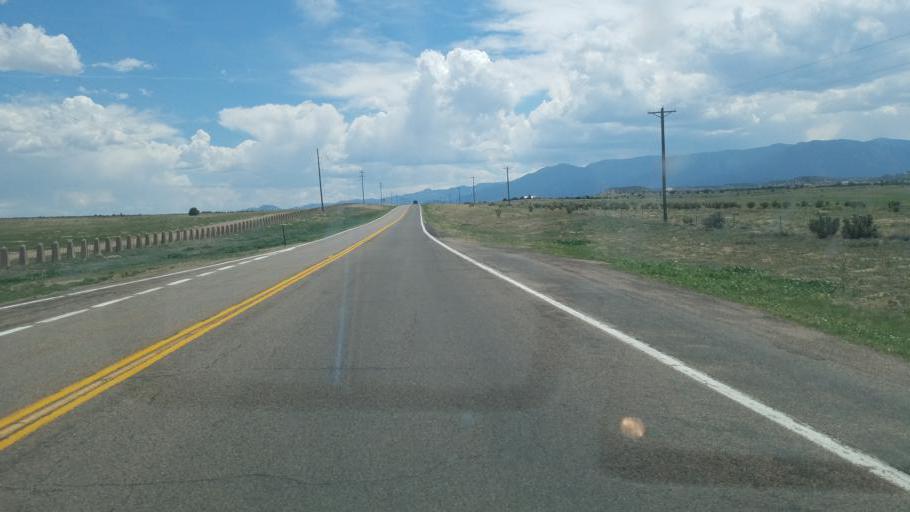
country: US
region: Colorado
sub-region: Fremont County
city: Florence
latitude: 38.3583
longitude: -105.1072
